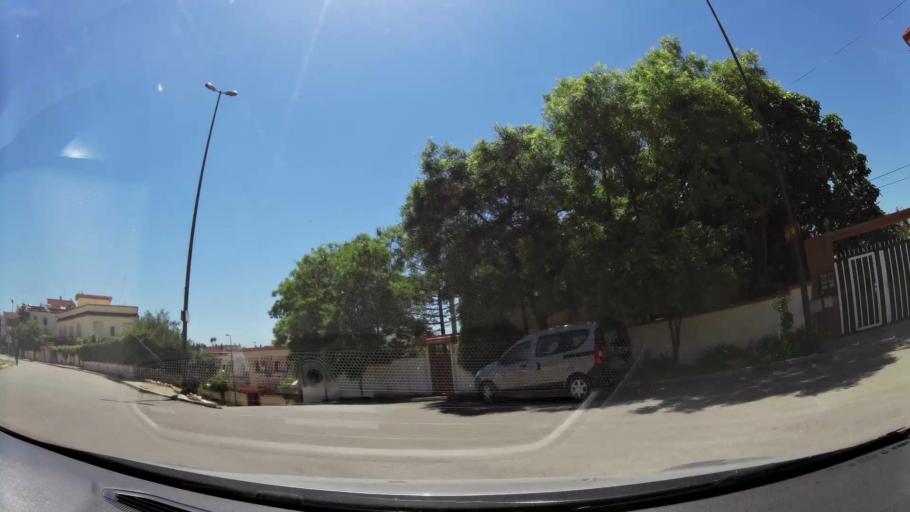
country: MA
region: Meknes-Tafilalet
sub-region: Meknes
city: Meknes
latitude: 33.8870
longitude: -5.5444
